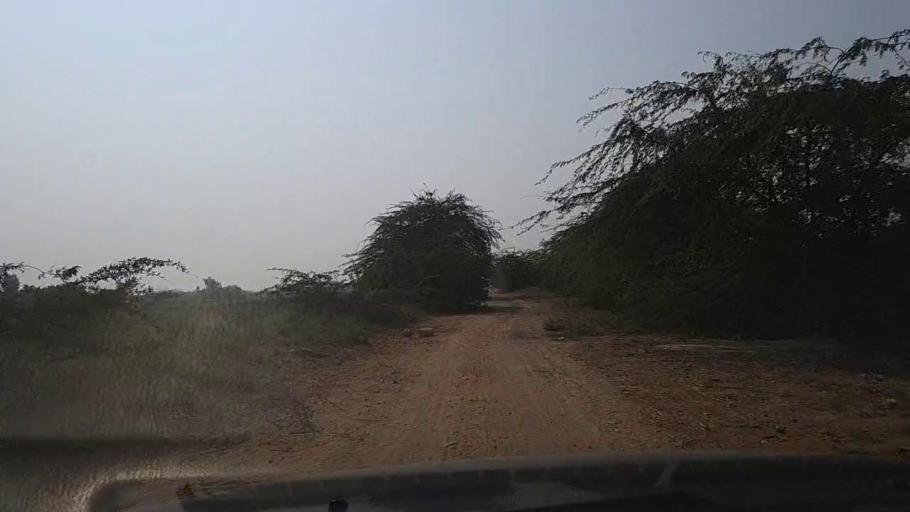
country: PK
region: Sindh
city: Thatta
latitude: 24.7760
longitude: 67.8317
